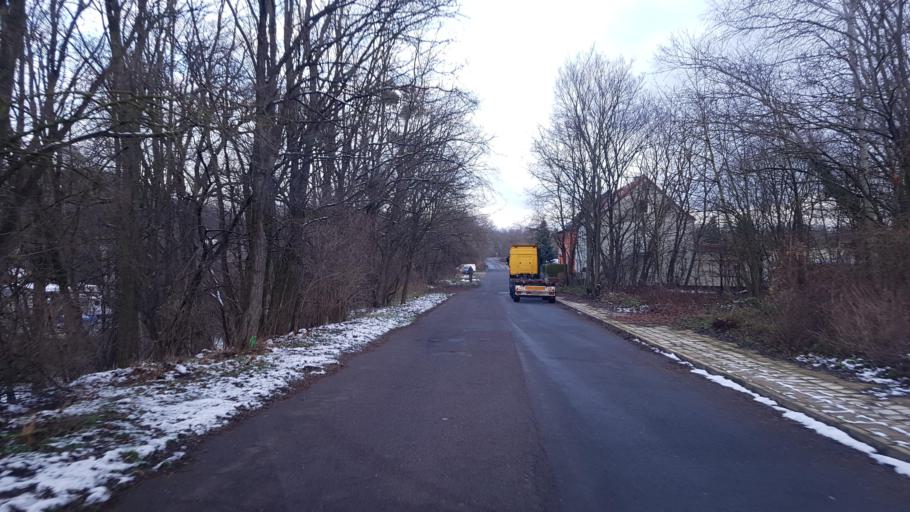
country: DE
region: Brandenburg
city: Petershagen
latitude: 52.4897
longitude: 13.7918
